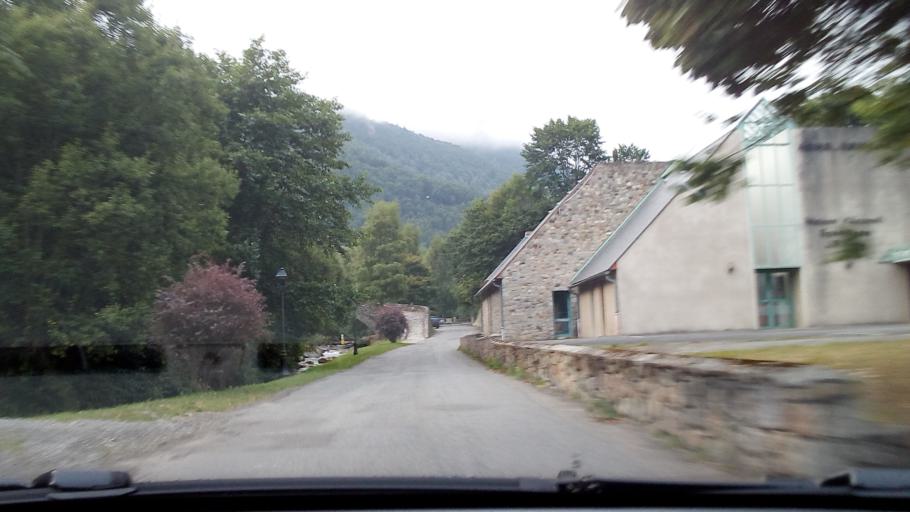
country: FR
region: Midi-Pyrenees
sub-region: Departement des Hautes-Pyrenees
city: Cauterets
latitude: 42.9508
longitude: -0.2158
